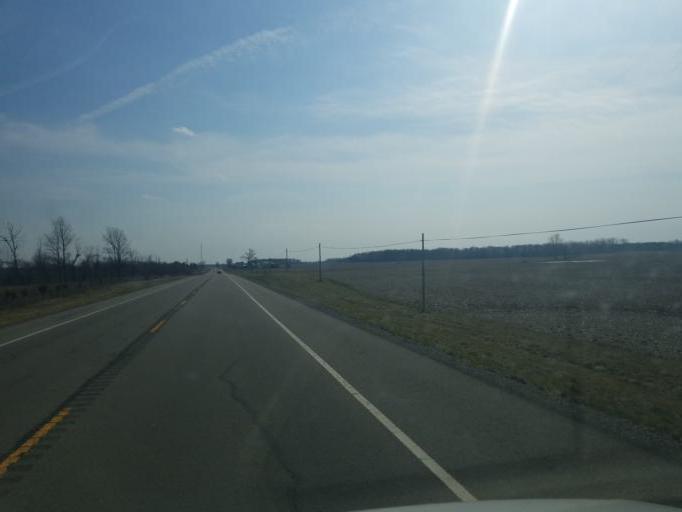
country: US
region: Ohio
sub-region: Logan County
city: Northwood
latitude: 40.5301
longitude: -83.6801
